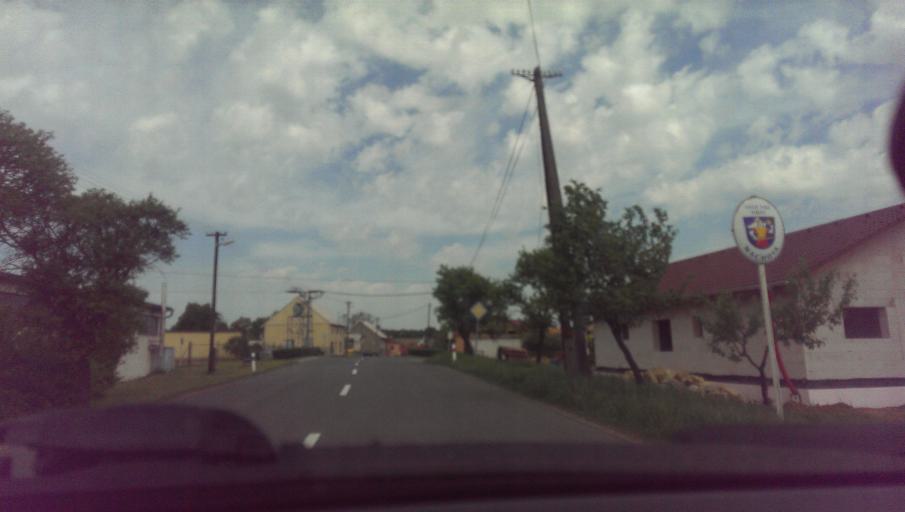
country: CZ
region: Zlin
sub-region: Okres Zlin
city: Otrokovice
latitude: 49.2508
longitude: 17.5430
